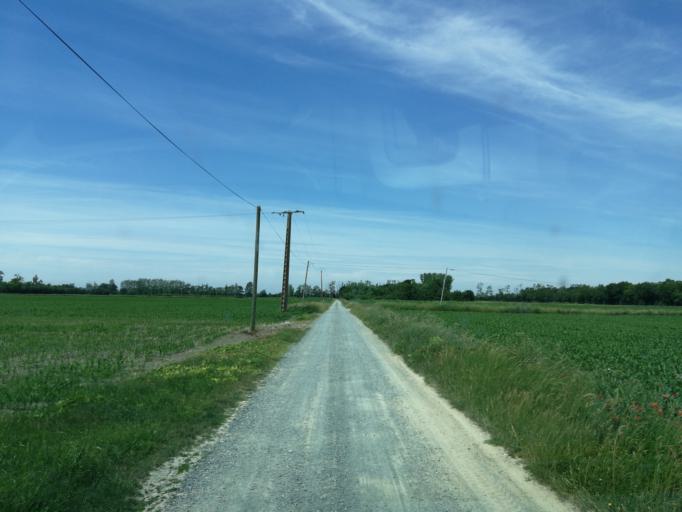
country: FR
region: Poitou-Charentes
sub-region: Departement de la Charente-Maritime
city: Marans
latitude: 46.3637
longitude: -0.9553
